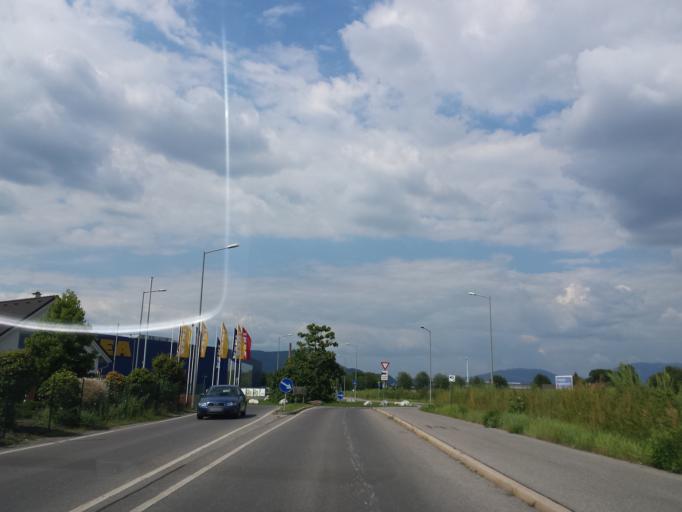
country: AT
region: Styria
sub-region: Politischer Bezirk Graz-Umgebung
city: Feldkirchen bei Graz
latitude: 47.0323
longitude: 15.4252
